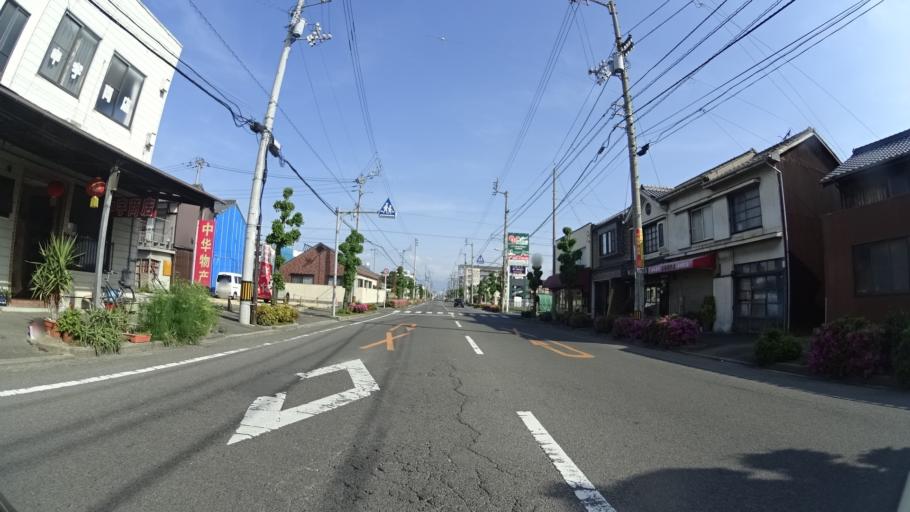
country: JP
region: Ehime
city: Saijo
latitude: 34.0628
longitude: 133.0098
